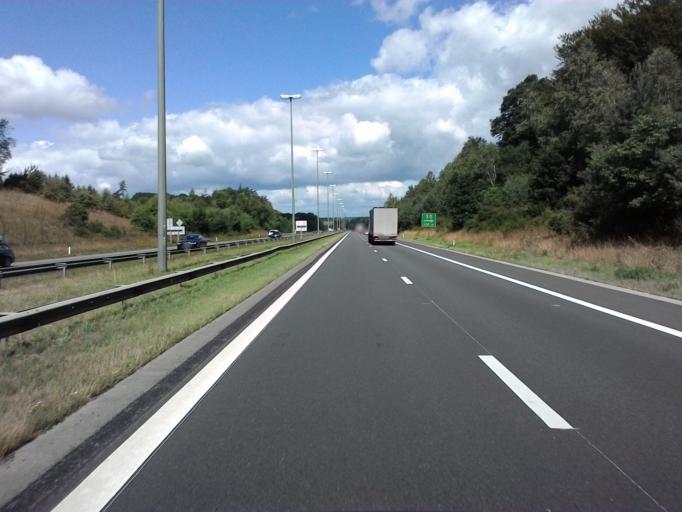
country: BE
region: Wallonia
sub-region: Province du Luxembourg
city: Arlon
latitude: 49.6794
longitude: 5.7600
